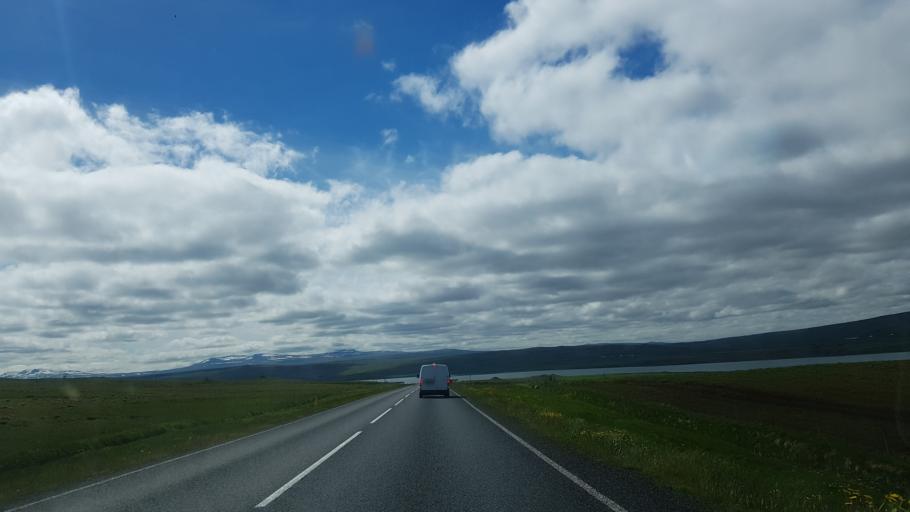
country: IS
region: West
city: Borgarnes
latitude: 65.2742
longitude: -21.0767
